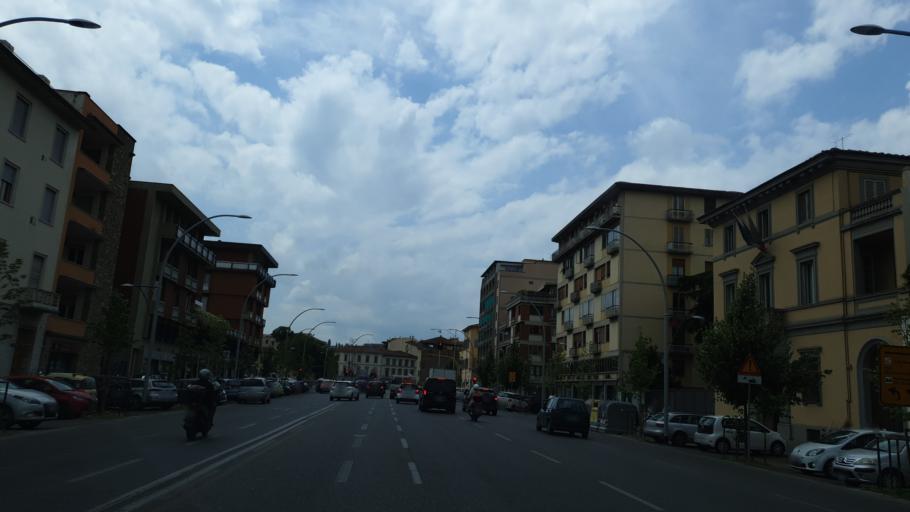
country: IT
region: Tuscany
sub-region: Province of Florence
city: Florence
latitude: 43.7799
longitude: 11.2414
